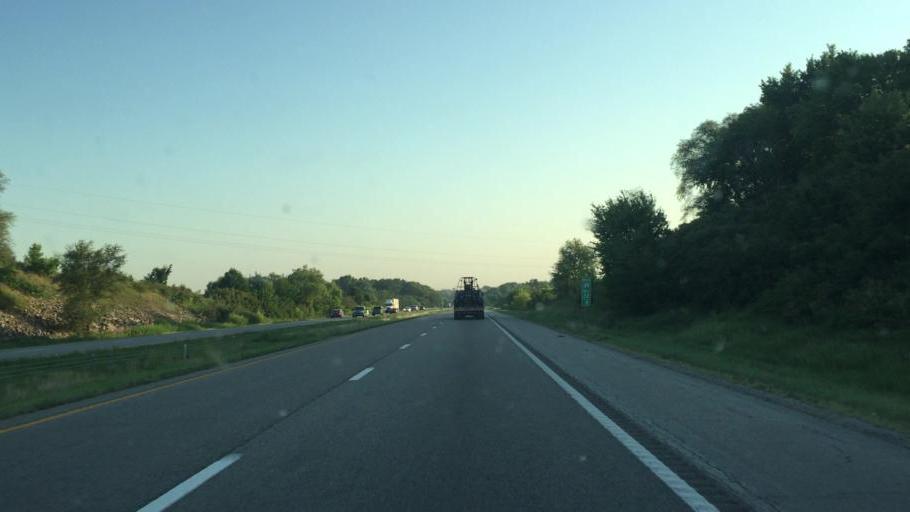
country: US
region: Missouri
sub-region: Platte County
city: Weston
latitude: 39.5577
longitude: -94.7879
